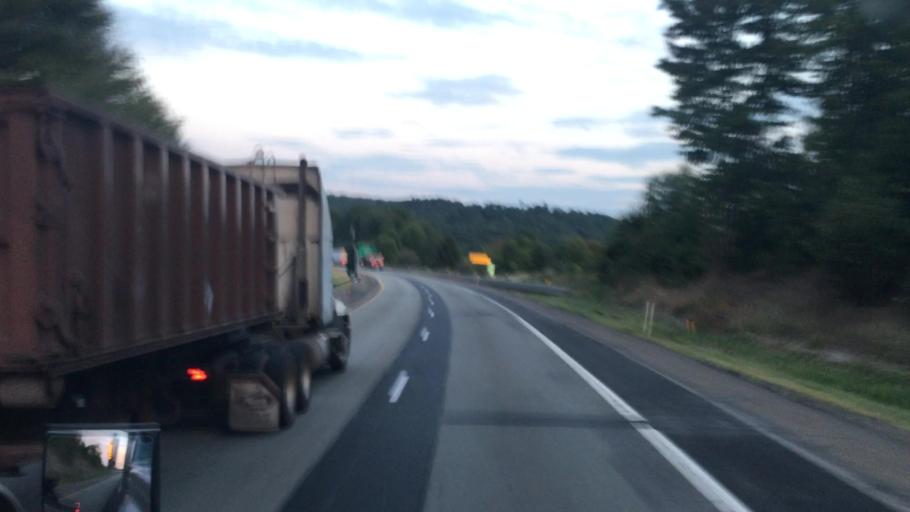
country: US
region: Pennsylvania
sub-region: Clarion County
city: Clarion
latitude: 41.1803
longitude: -79.3804
